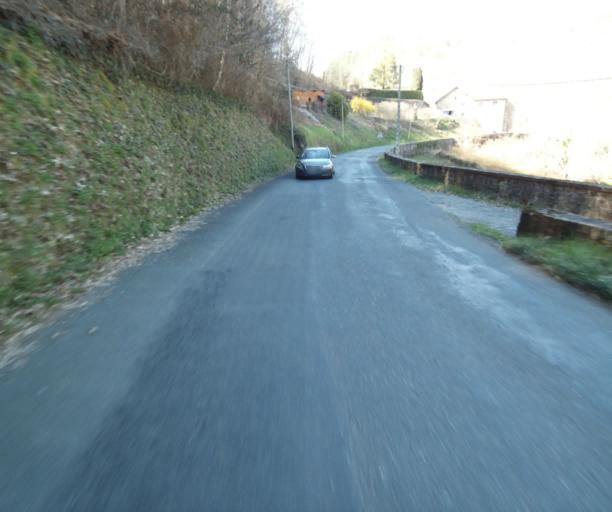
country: FR
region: Limousin
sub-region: Departement de la Correze
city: Tulle
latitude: 45.2726
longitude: 1.7382
